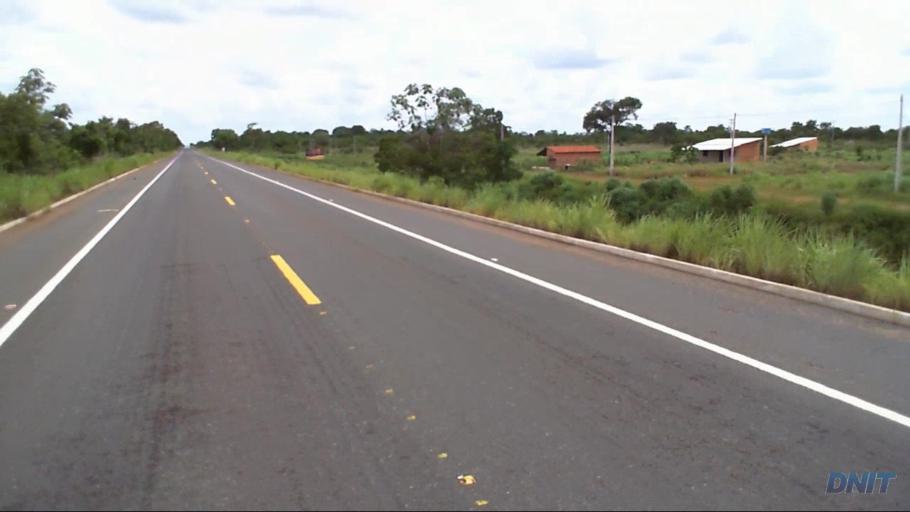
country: BR
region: Goias
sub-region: Sao Miguel Do Araguaia
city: Sao Miguel do Araguaia
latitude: -13.2453
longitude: -50.5352
